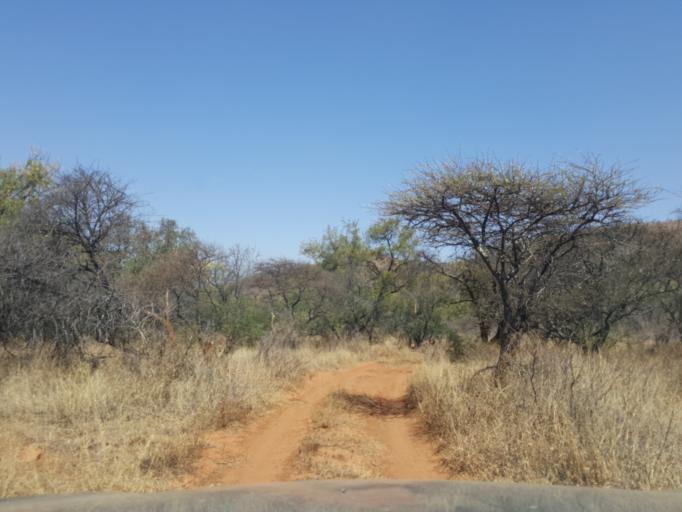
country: BW
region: South East
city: Lobatse
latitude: -25.1442
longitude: 25.6696
